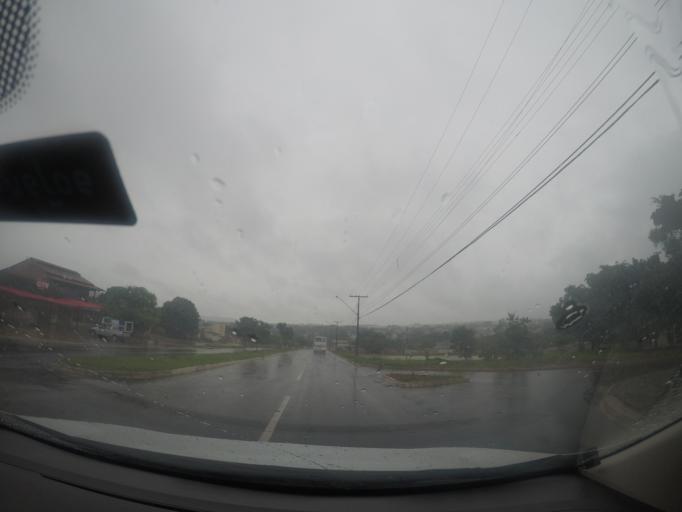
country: BR
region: Goias
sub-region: Goiania
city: Goiania
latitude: -16.6103
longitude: -49.3369
